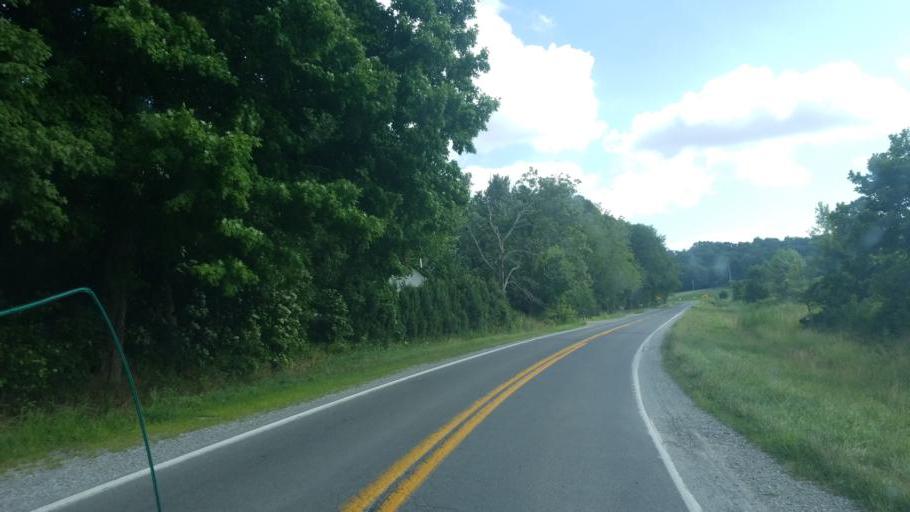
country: US
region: Illinois
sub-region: Union County
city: Cobden
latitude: 37.5511
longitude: -89.2641
